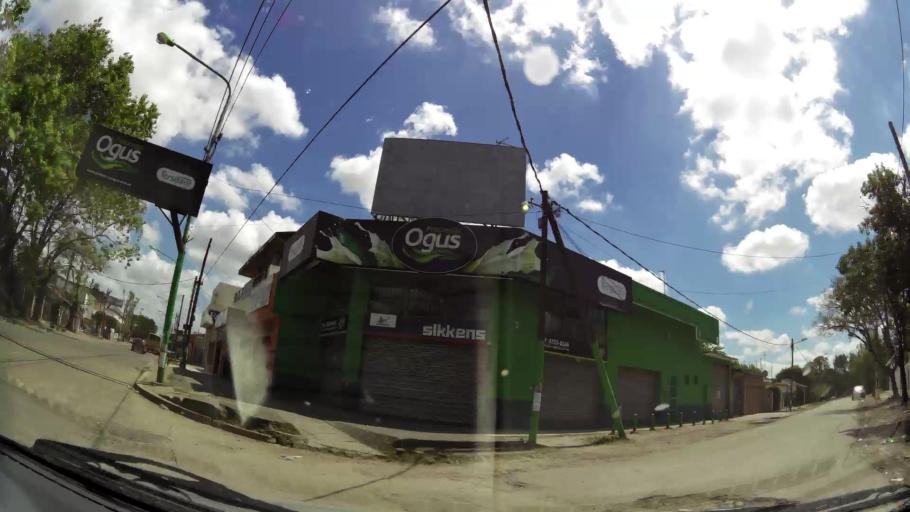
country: AR
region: Buenos Aires
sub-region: Partido de Quilmes
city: Quilmes
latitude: -34.8089
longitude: -58.2552
